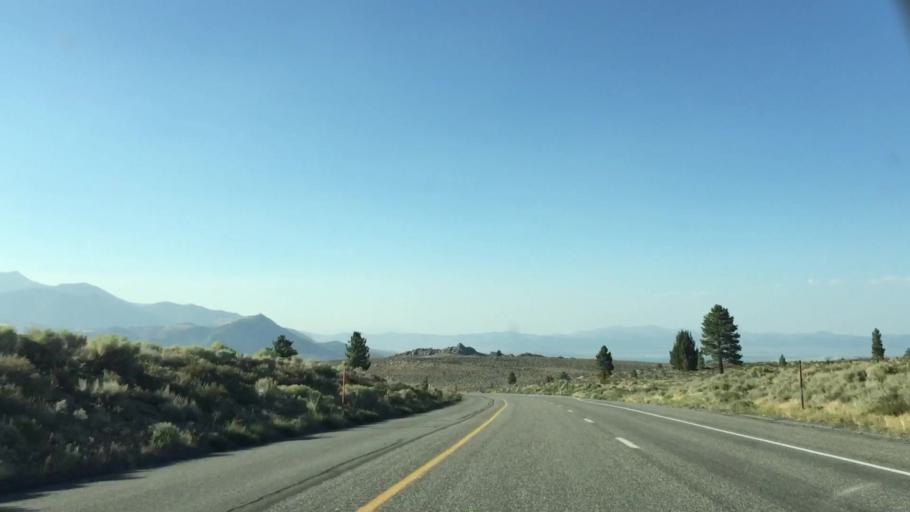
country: US
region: California
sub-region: Mono County
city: Mammoth Lakes
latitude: 37.8370
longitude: -119.0699
